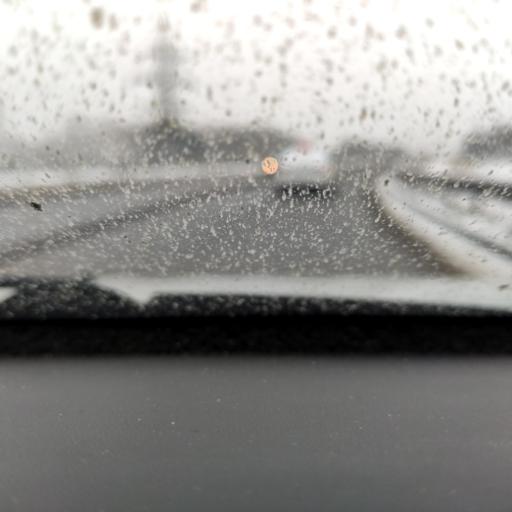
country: RU
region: Perm
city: Kondratovo
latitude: 58.0319
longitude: 56.0510
